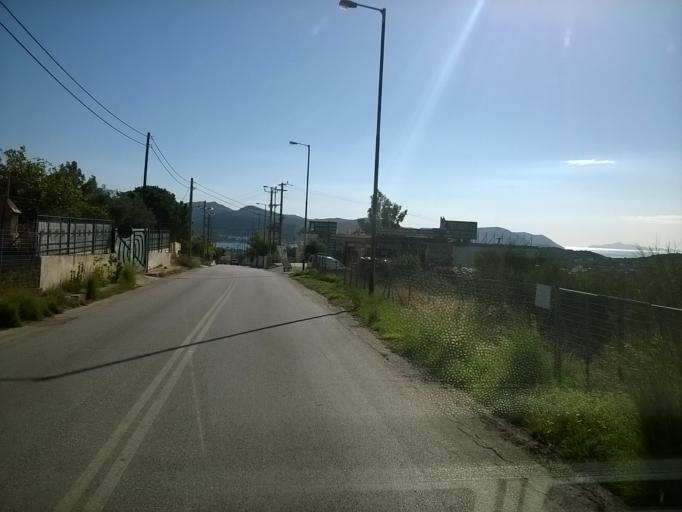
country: GR
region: Attica
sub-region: Nomarchia Anatolikis Attikis
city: Anavyssos
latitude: 37.7390
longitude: 23.9283
